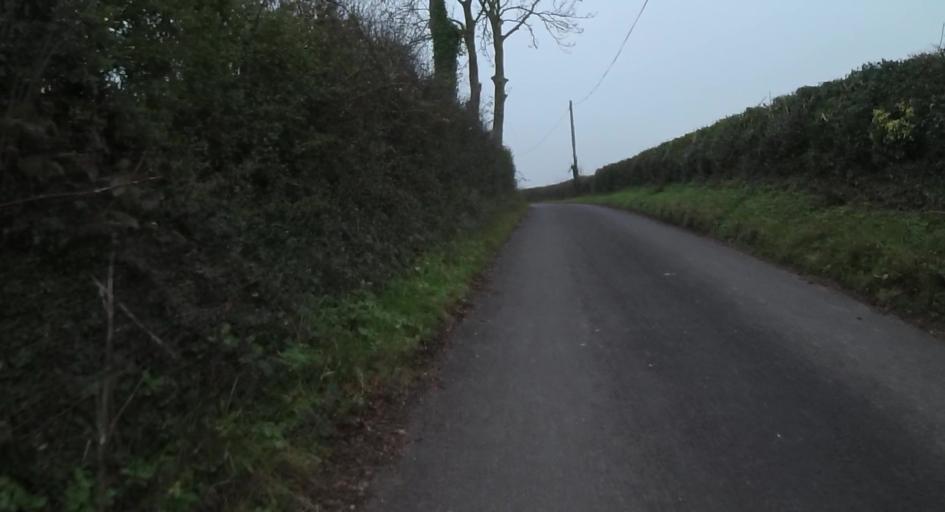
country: GB
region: England
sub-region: Hampshire
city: Kings Worthy
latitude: 51.0768
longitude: -1.2856
